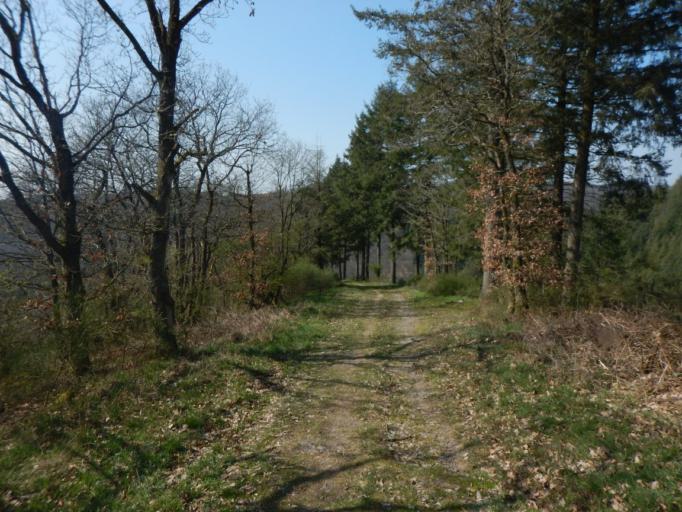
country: LU
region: Diekirch
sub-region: Canton de Diekirch
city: Bourscheid
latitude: 49.9491
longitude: 6.0720
